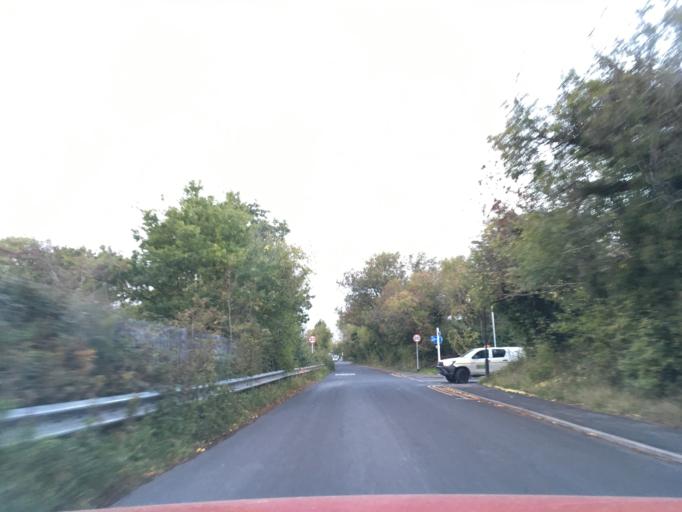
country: GB
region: England
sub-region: South Gloucestershire
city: Almondsbury
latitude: 51.5298
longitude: -2.5648
